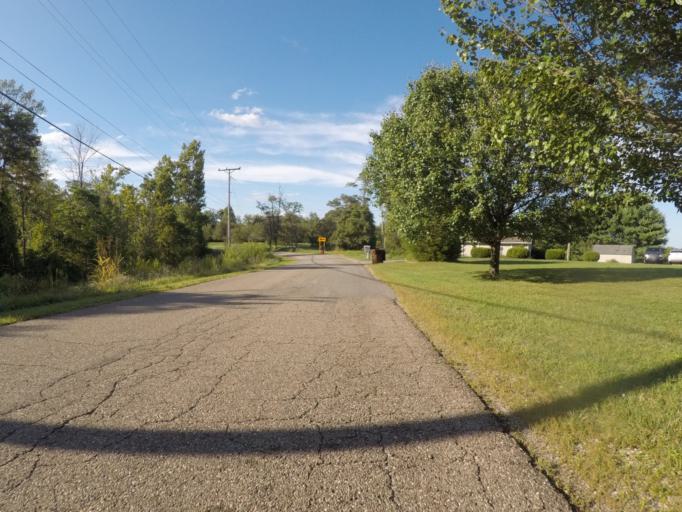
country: US
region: West Virginia
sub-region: Cabell County
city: Huntington
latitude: 38.4621
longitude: -82.4609
